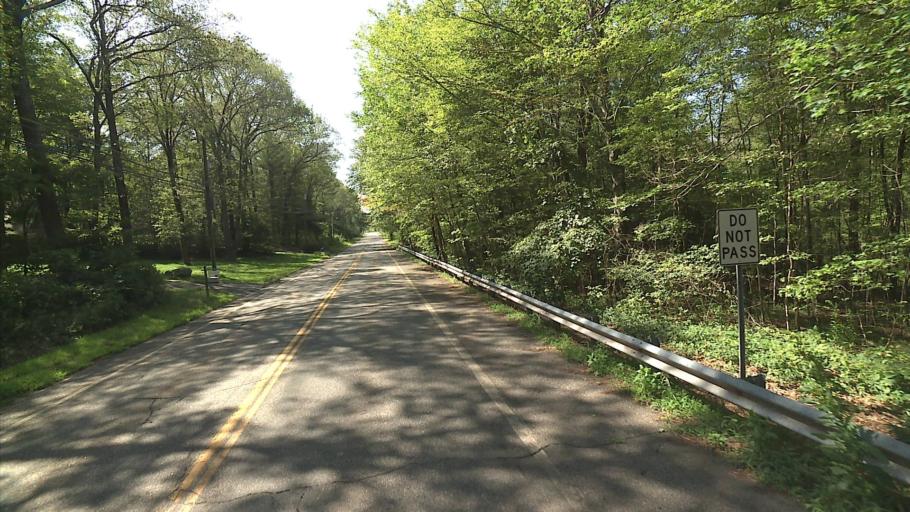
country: US
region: Connecticut
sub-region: Tolland County
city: Storrs
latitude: 41.8970
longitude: -72.1700
